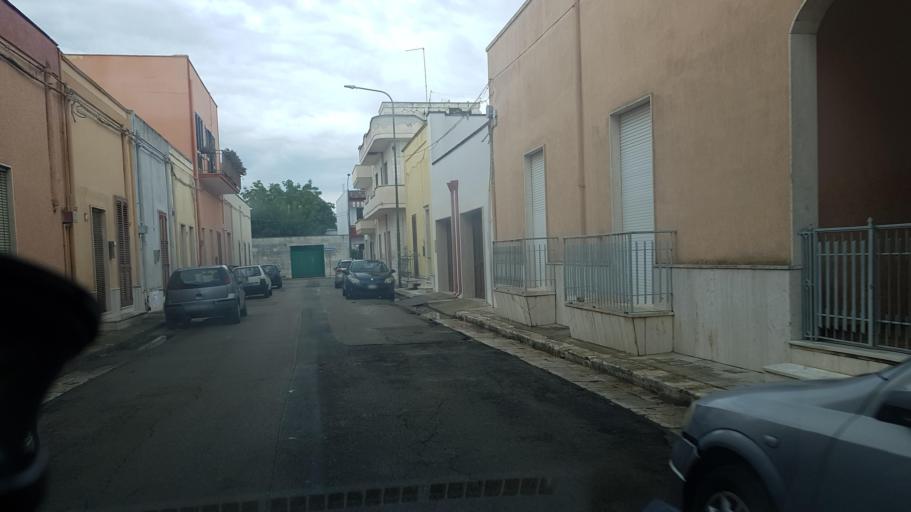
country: IT
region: Apulia
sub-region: Provincia di Lecce
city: Salice Salentino
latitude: 40.3837
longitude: 17.9640
